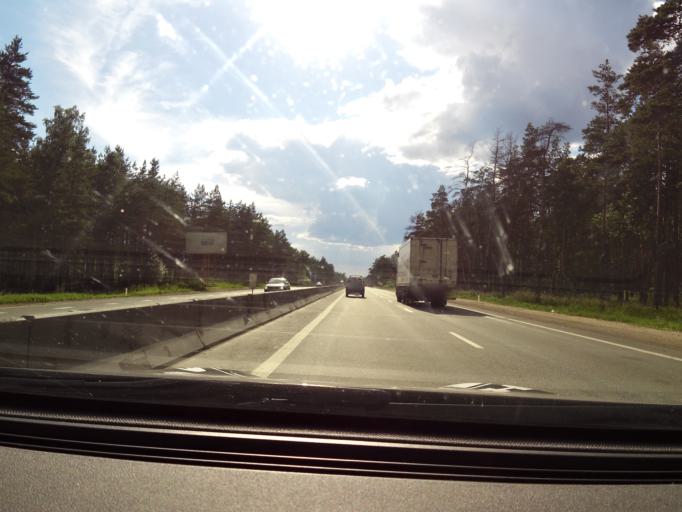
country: RU
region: Nizjnij Novgorod
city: Pyra
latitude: 56.2950
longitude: 43.3932
